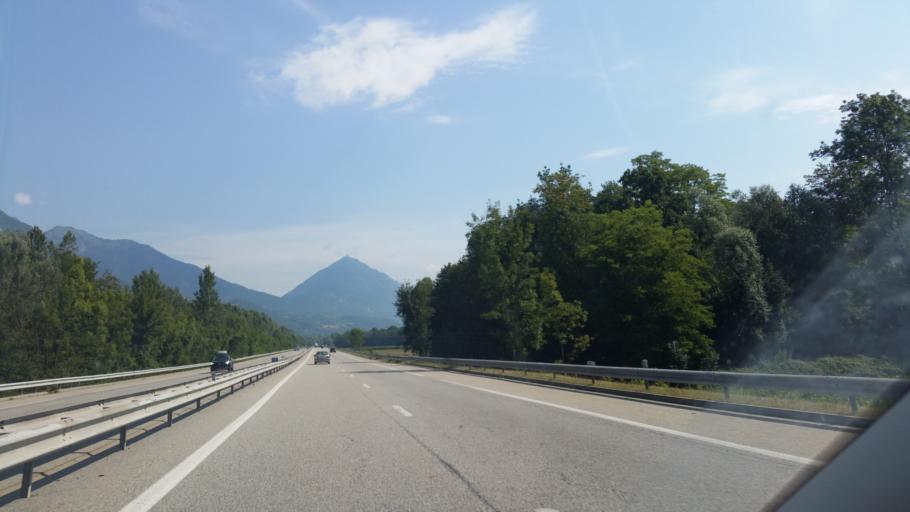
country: FR
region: Rhone-Alpes
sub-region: Departement de la Savoie
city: Gresy-sur-Isere
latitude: 45.5860
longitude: 6.2737
